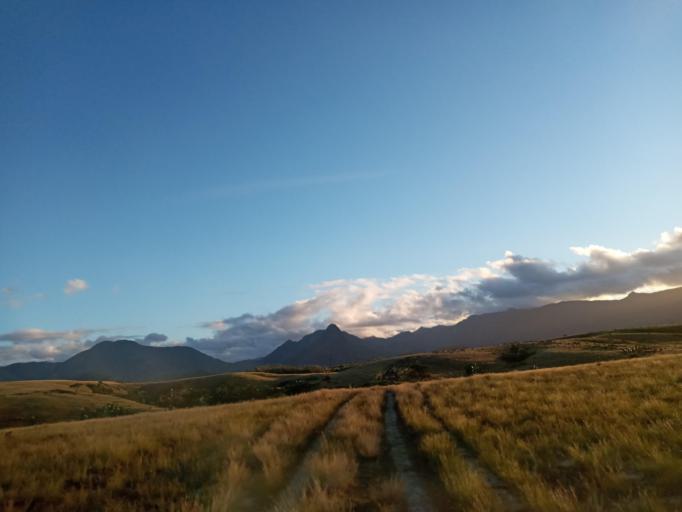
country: MG
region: Anosy
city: Fort Dauphin
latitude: -24.5146
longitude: 47.2478
